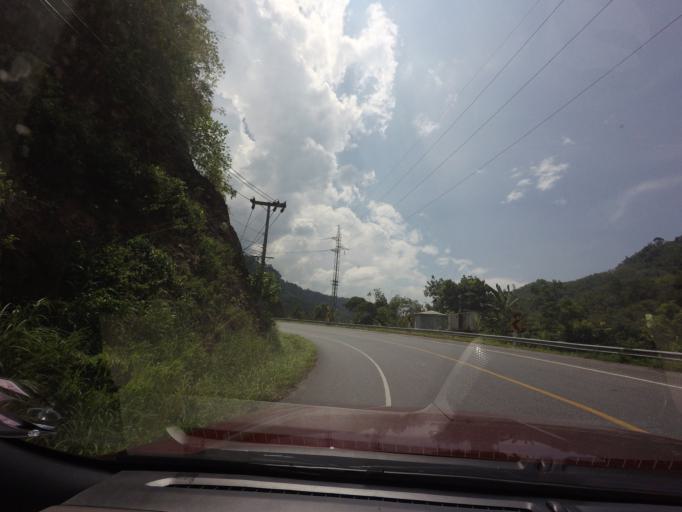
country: TH
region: Yala
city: Than To
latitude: 5.9940
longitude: 101.1929
